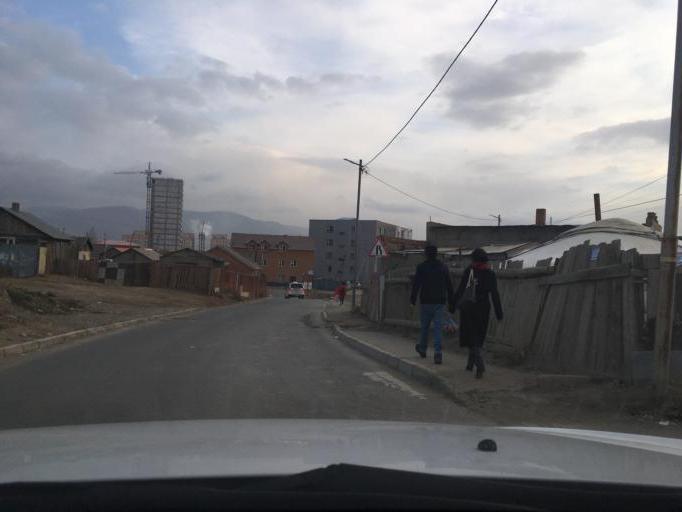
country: MN
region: Ulaanbaatar
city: Ulaanbaatar
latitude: 47.9253
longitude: 106.8566
